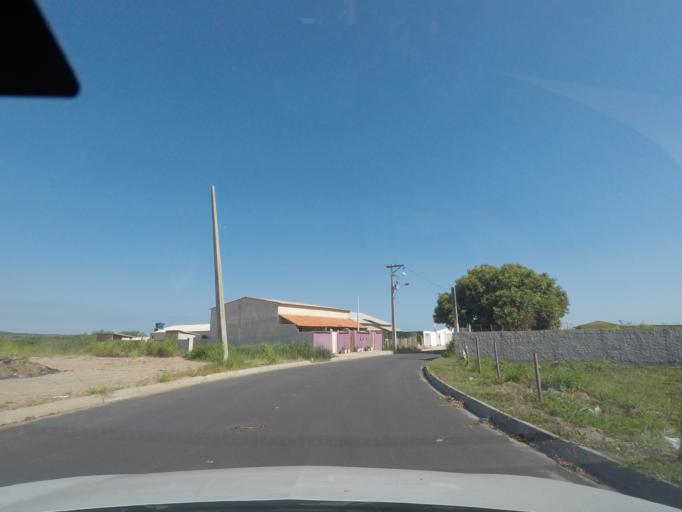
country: BR
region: Rio de Janeiro
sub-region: Marica
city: Marica
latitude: -22.9572
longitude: -42.9249
